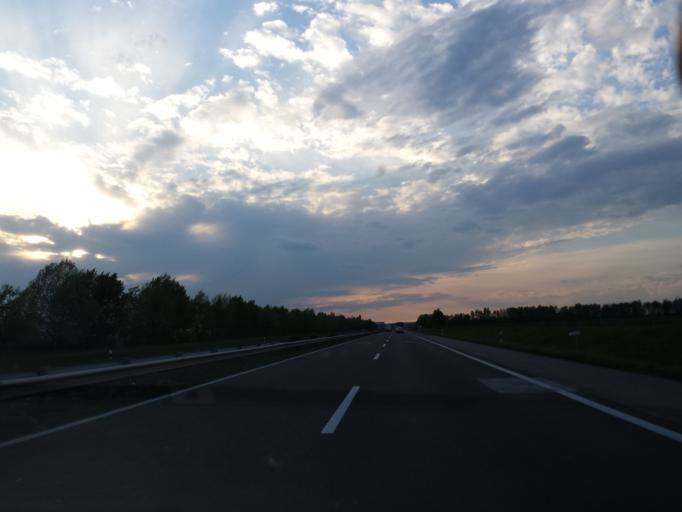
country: HU
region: Gyor-Moson-Sopron
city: Otteveny
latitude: 47.7225
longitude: 17.4594
